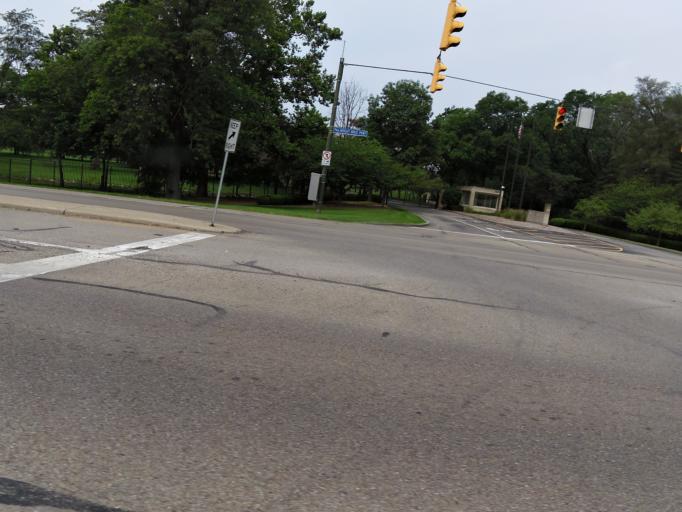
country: US
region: Ohio
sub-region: Montgomery County
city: Riverside
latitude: 39.7518
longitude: -84.1198
